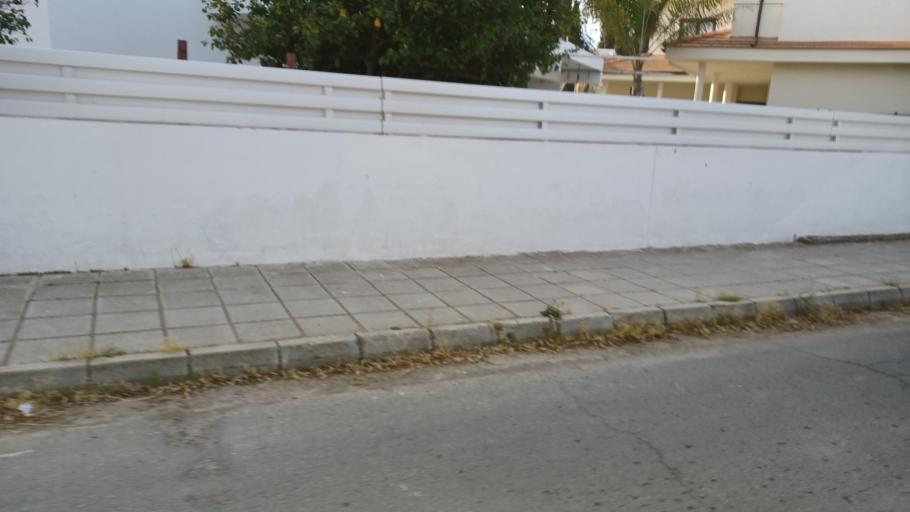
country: CY
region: Lefkosia
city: Mammari
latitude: 35.1717
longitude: 33.1983
